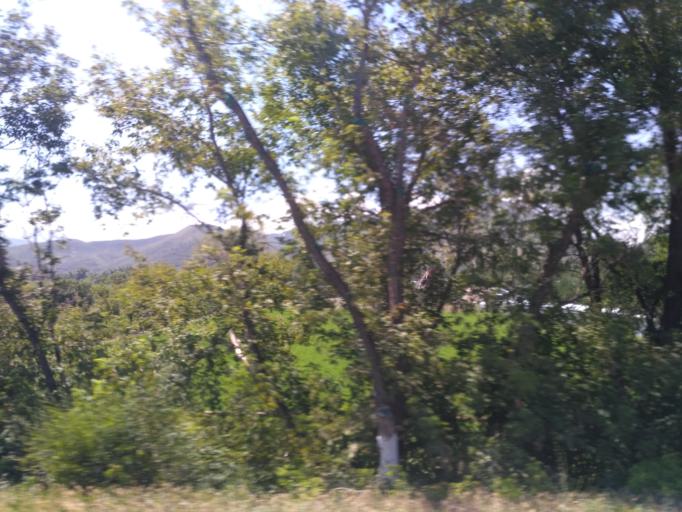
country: KZ
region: Almaty Oblysy
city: Burunday
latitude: 43.1664
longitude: 76.5892
